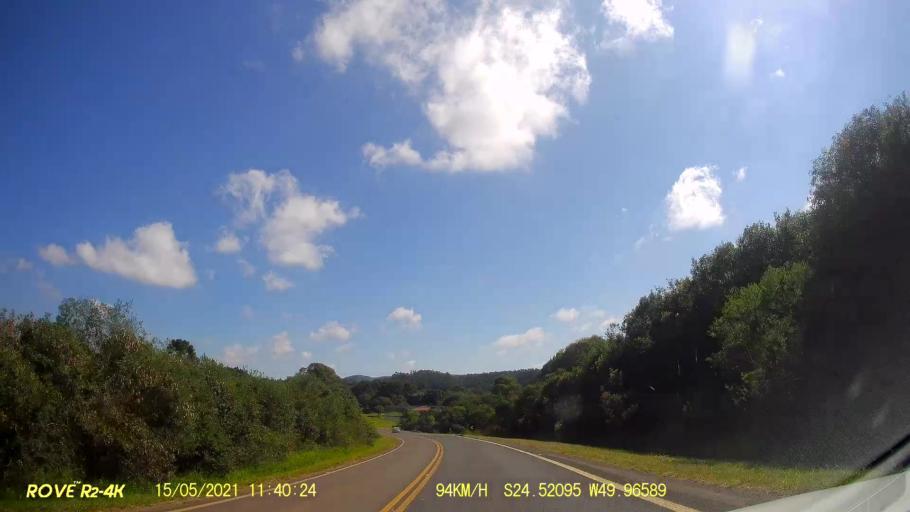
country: BR
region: Parana
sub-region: Pirai Do Sul
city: Pirai do Sul
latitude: -24.5209
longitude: -49.9659
